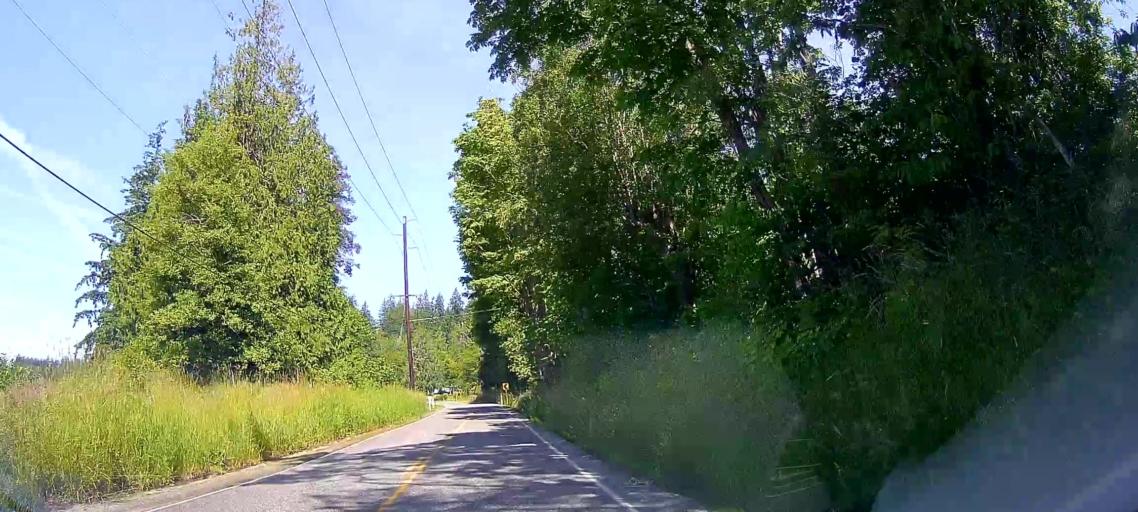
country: US
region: Washington
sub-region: Skagit County
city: Sedro-Woolley
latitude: 48.5335
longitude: -122.2874
